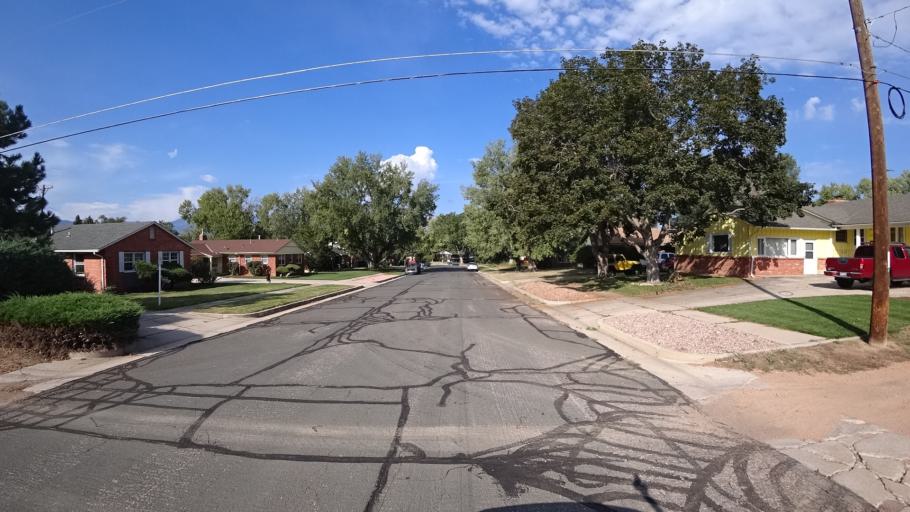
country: US
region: Colorado
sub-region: El Paso County
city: Colorado Springs
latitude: 38.8577
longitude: -104.7775
